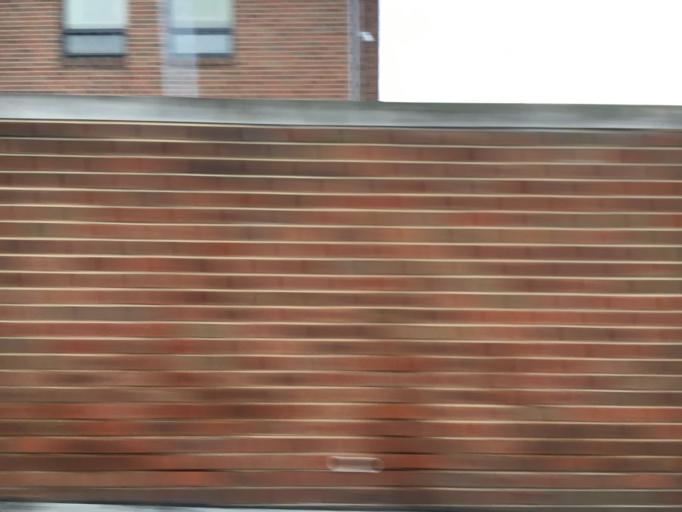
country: US
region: Pennsylvania
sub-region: Northampton County
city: Northampton
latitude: 40.6964
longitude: -75.4991
